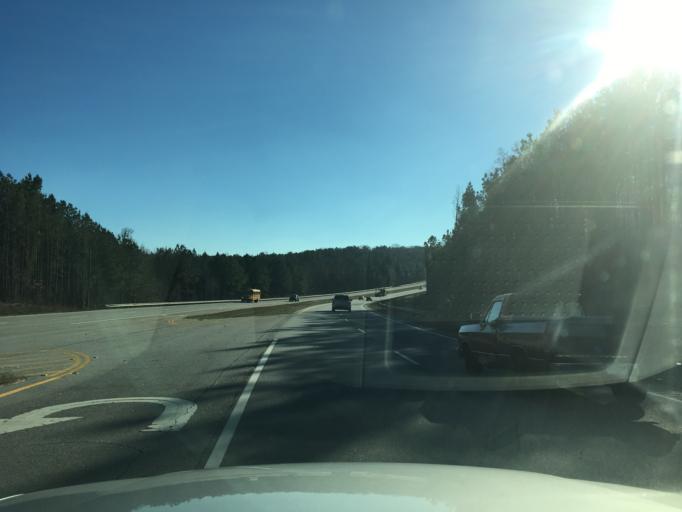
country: US
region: Georgia
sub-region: Carroll County
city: Carrollton
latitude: 33.4504
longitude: -85.1247
